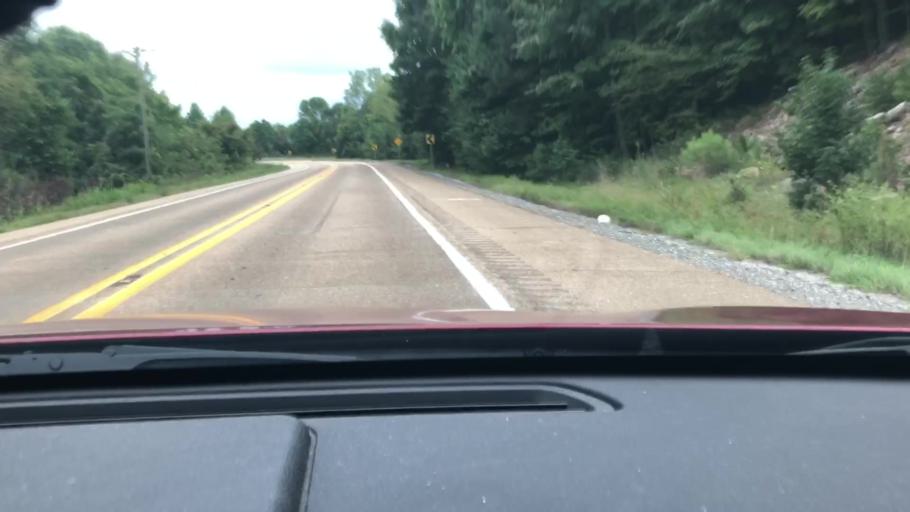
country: US
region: Arkansas
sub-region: Miller County
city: Texarkana
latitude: 33.4148
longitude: -93.8104
